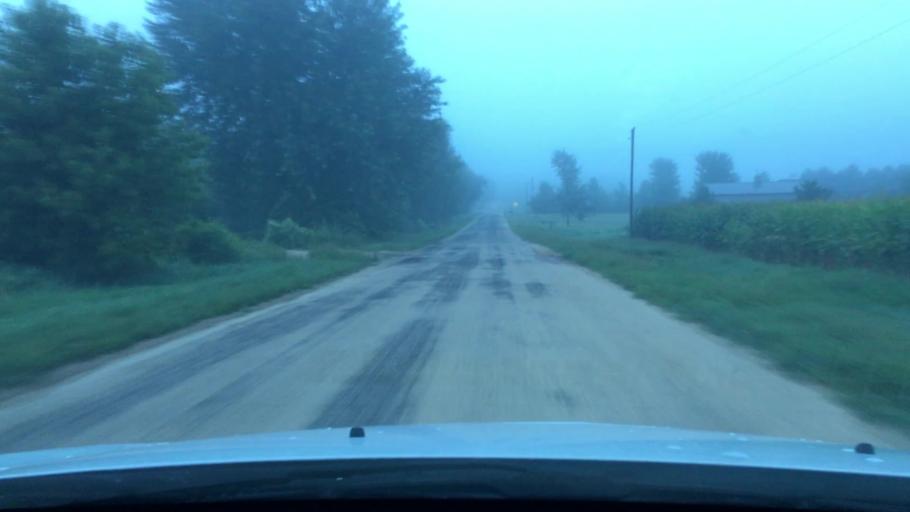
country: US
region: Illinois
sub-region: Ogle County
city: Rochelle
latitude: 41.8507
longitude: -88.9811
